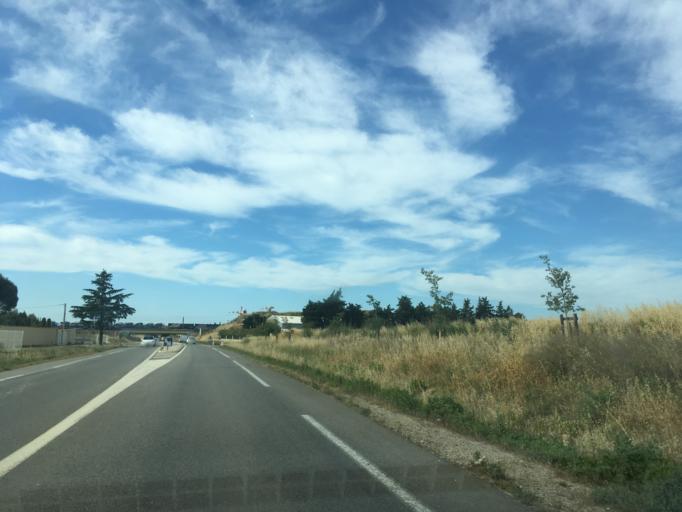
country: FR
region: Languedoc-Roussillon
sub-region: Departement du Gard
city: Bouillargues
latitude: 43.7836
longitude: 4.4301
